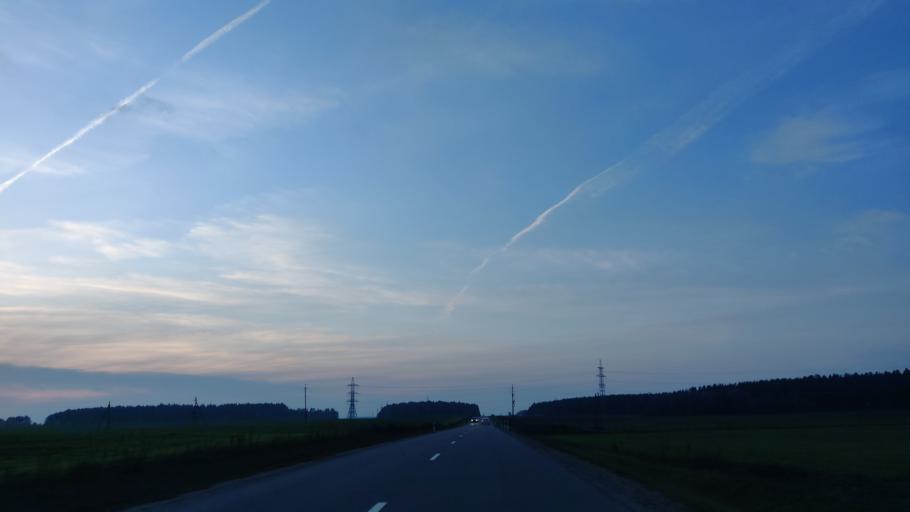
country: LT
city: Lentvaris
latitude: 54.5938
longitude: 25.0425
